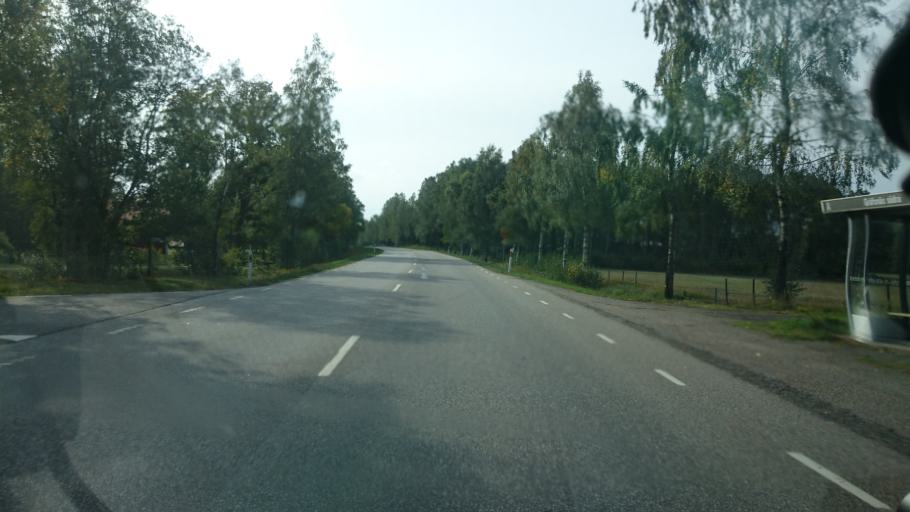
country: SE
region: Vaestra Goetaland
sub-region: Alingsas Kommun
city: Sollebrunn
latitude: 58.0754
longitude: 12.4826
